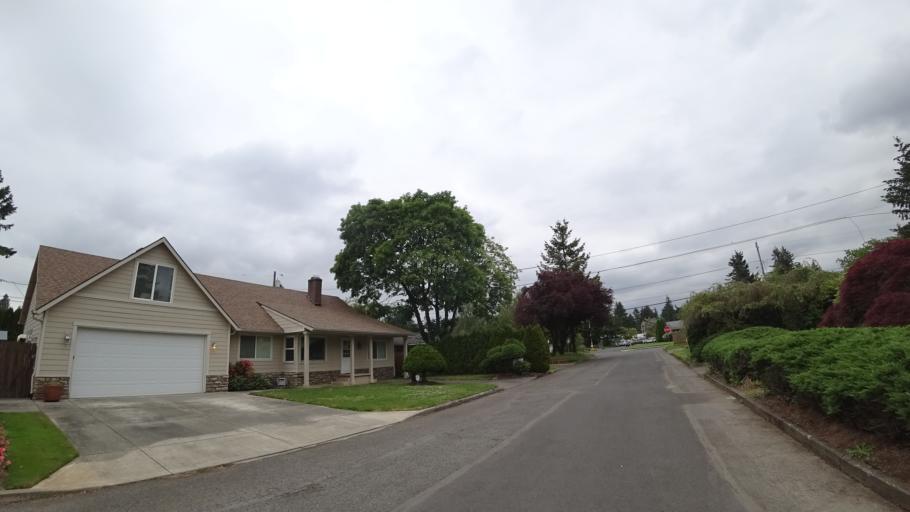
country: US
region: Oregon
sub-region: Multnomah County
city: Lents
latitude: 45.5121
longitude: -122.5256
